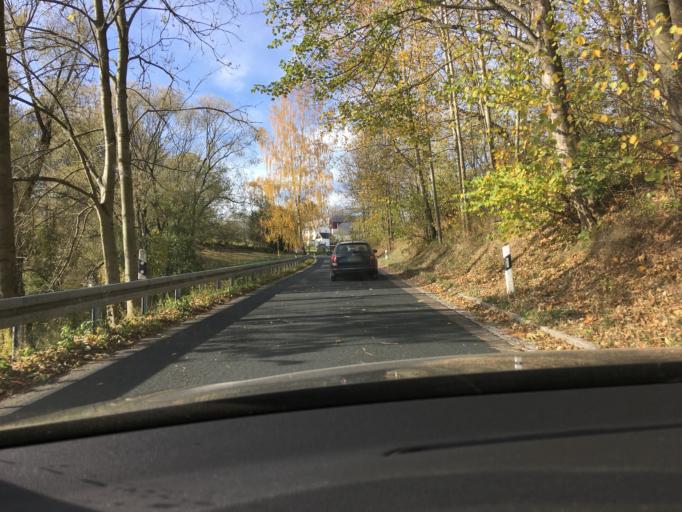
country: DE
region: Saxony
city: Barenstein
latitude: 50.8168
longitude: 13.8222
